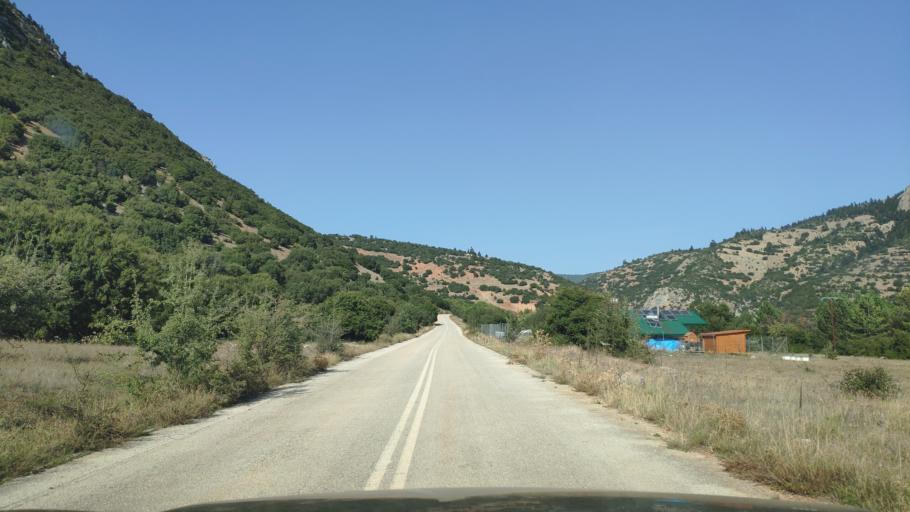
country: GR
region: West Greece
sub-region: Nomos Achaias
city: Aiyira
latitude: 37.9649
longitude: 22.3466
